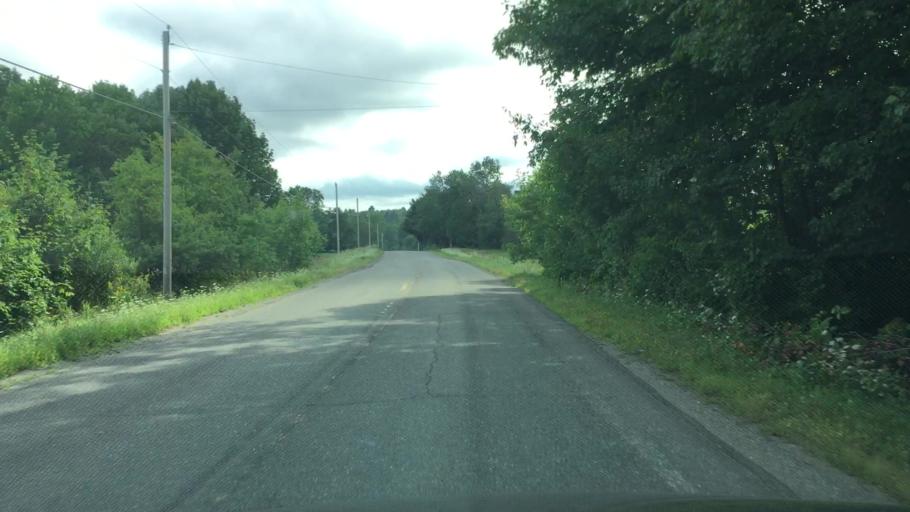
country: US
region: Maine
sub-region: Penobscot County
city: Hampden
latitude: 44.7196
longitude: -68.8675
